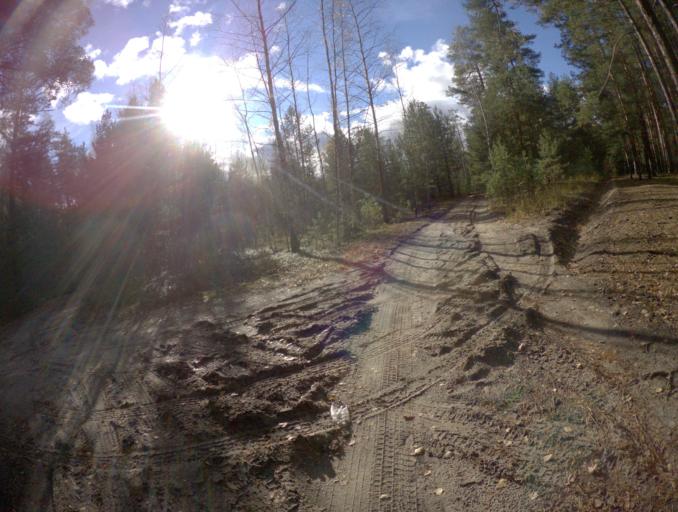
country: RU
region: Vladimir
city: Raduzhnyy
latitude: 56.0591
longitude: 40.3295
